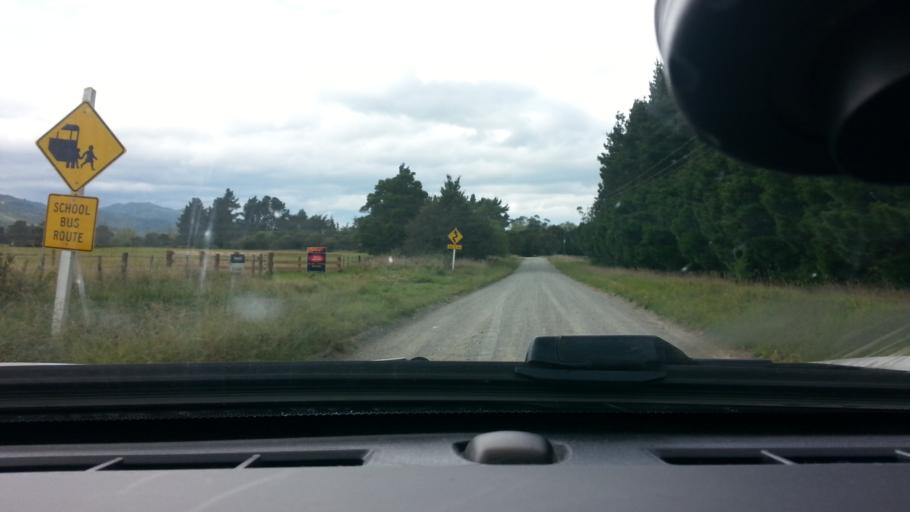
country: NZ
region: Wellington
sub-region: Masterton District
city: Masterton
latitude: -41.0637
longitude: 175.4005
